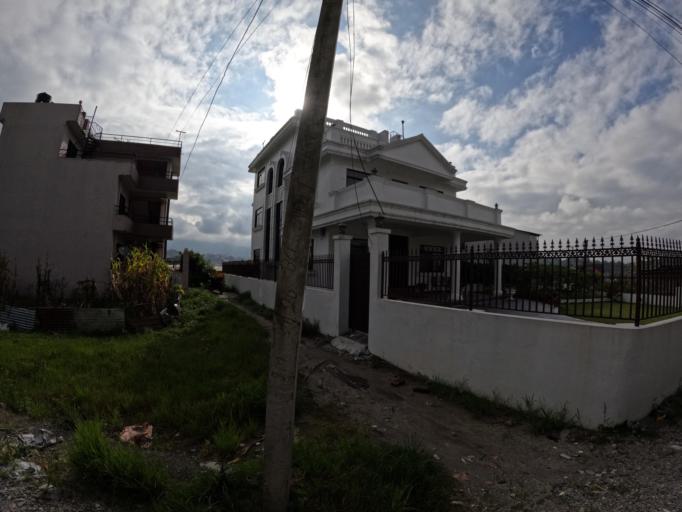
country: NP
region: Central Region
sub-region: Bagmati Zone
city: Kathmandu
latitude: 27.7646
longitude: 85.3340
